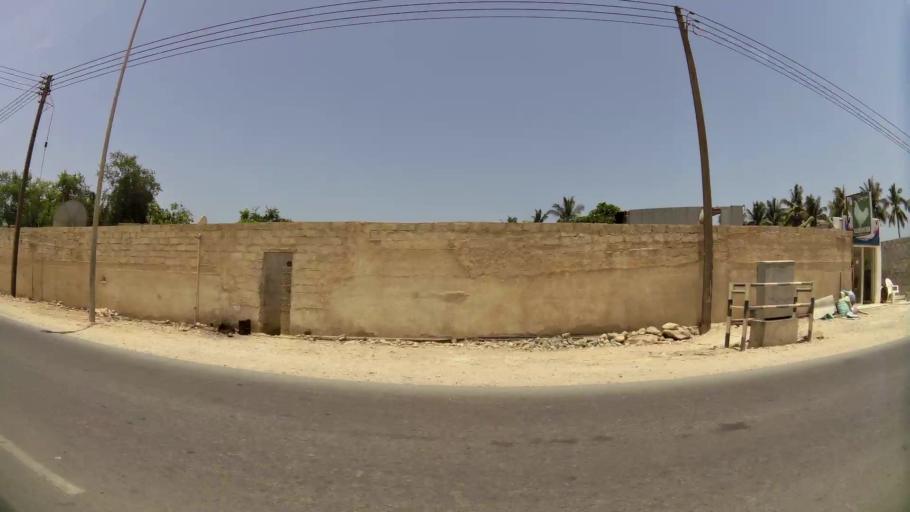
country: OM
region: Zufar
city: Salalah
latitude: 17.0107
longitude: 54.1077
